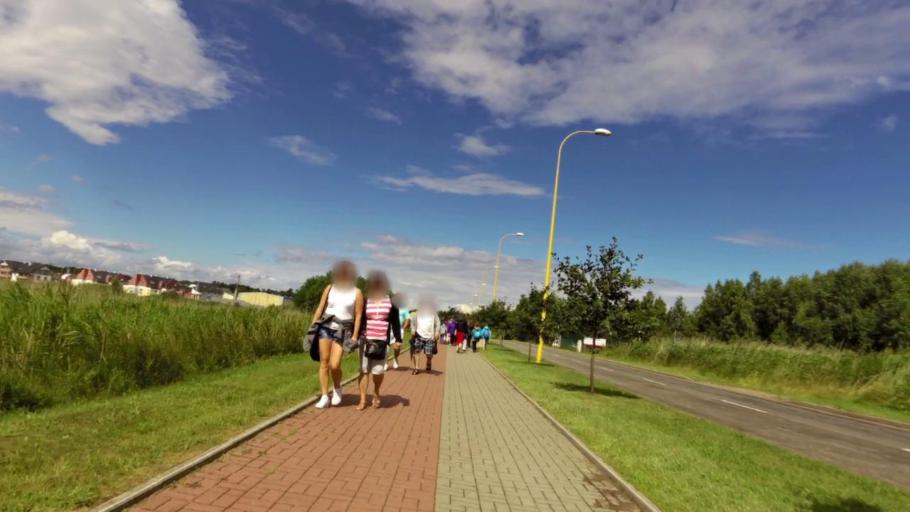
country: PL
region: West Pomeranian Voivodeship
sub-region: Powiat slawienski
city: Darlowo
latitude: 54.4433
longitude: 16.4013
